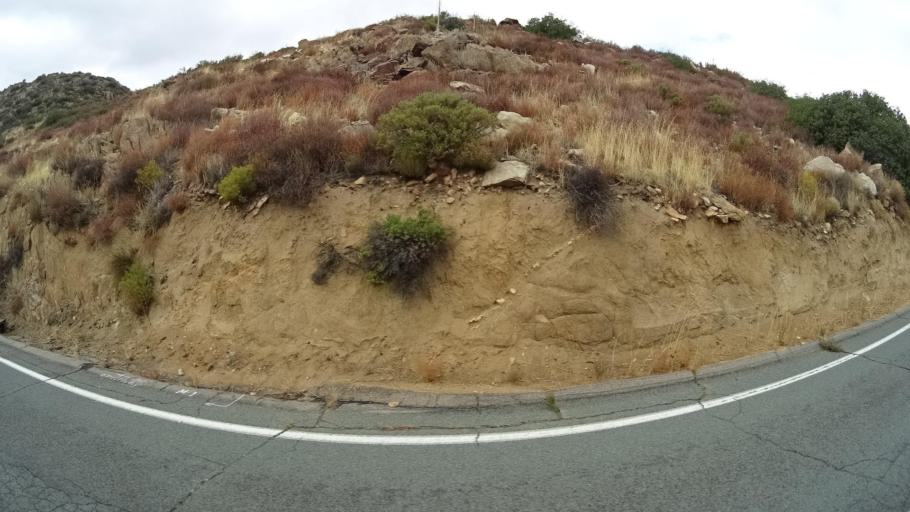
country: US
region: California
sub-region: San Diego County
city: Pine Valley
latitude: 32.7456
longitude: -116.4519
